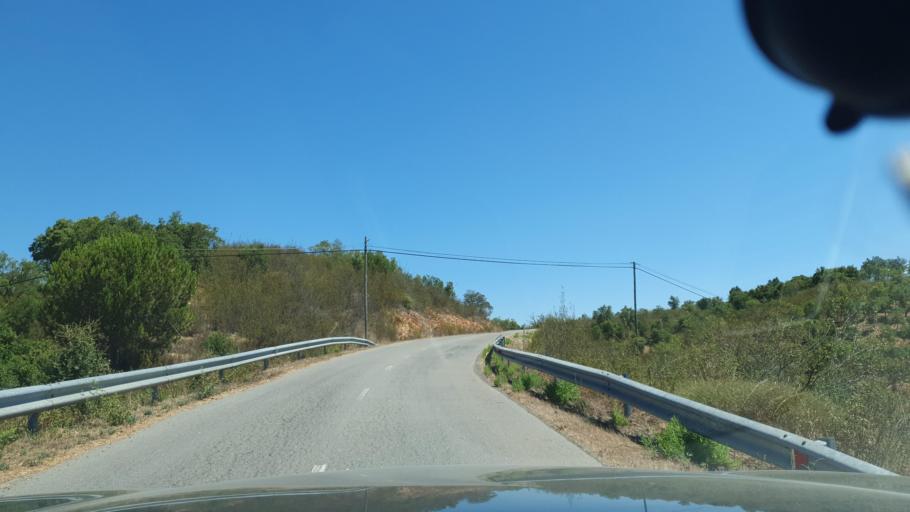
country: PT
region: Beja
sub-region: Odemira
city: Odemira
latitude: 37.5525
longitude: -8.4356
